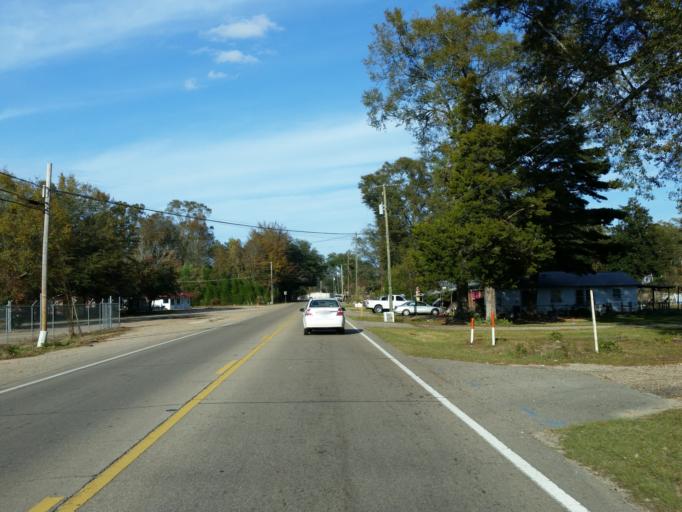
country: US
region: Mississippi
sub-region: Jones County
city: Ellisville
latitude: 31.6422
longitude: -89.1786
